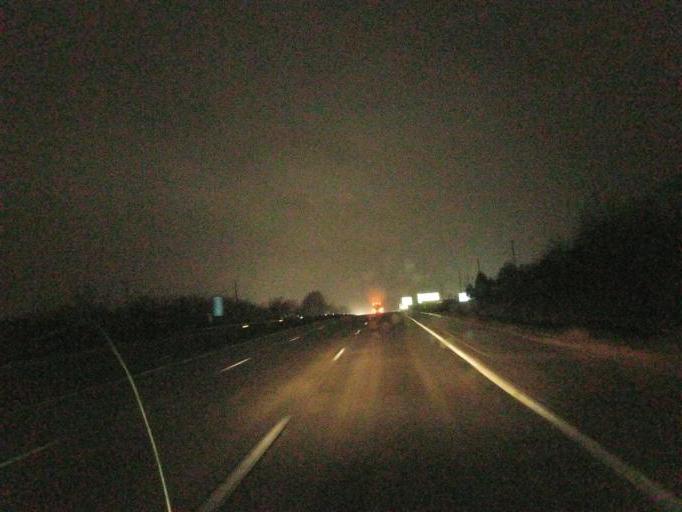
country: US
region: Missouri
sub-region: Saint Louis County
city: Eureka
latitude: 38.5049
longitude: -90.6134
